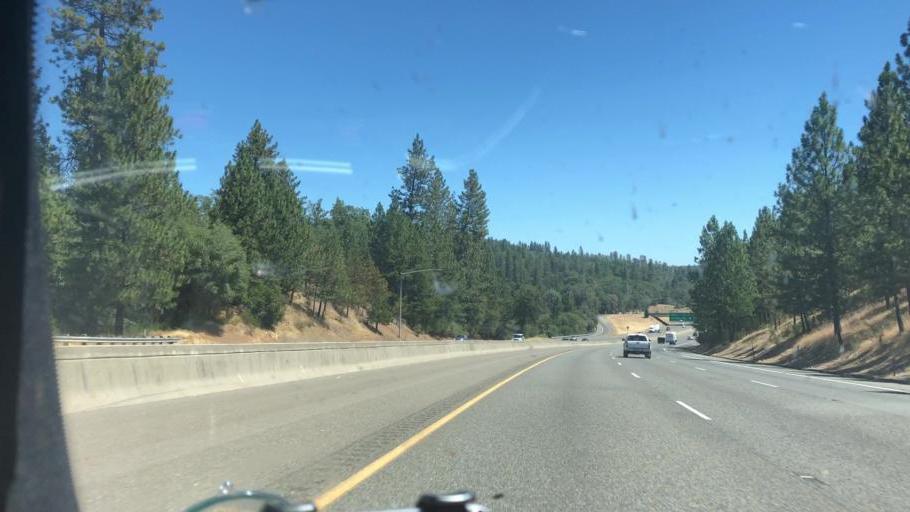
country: US
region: California
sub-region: Placer County
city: North Auburn
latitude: 38.9534
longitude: -121.0379
